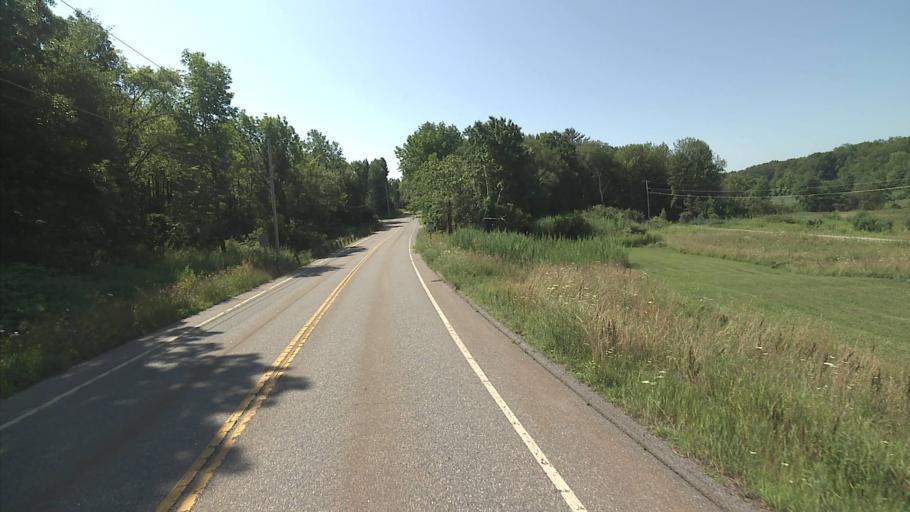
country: US
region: Connecticut
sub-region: Litchfield County
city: New Preston
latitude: 41.7753
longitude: -73.3534
